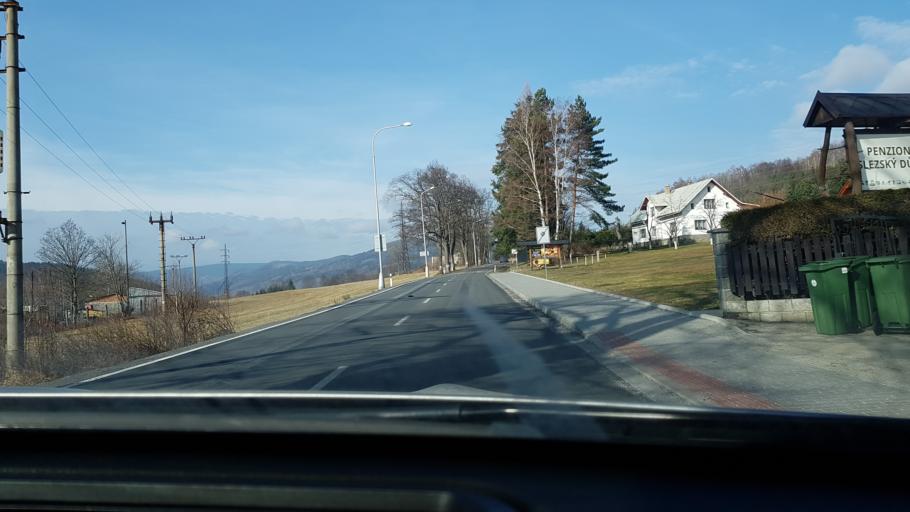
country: CZ
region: Olomoucky
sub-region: Okres Jesenik
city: Jesenik
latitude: 50.2271
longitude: 17.1813
